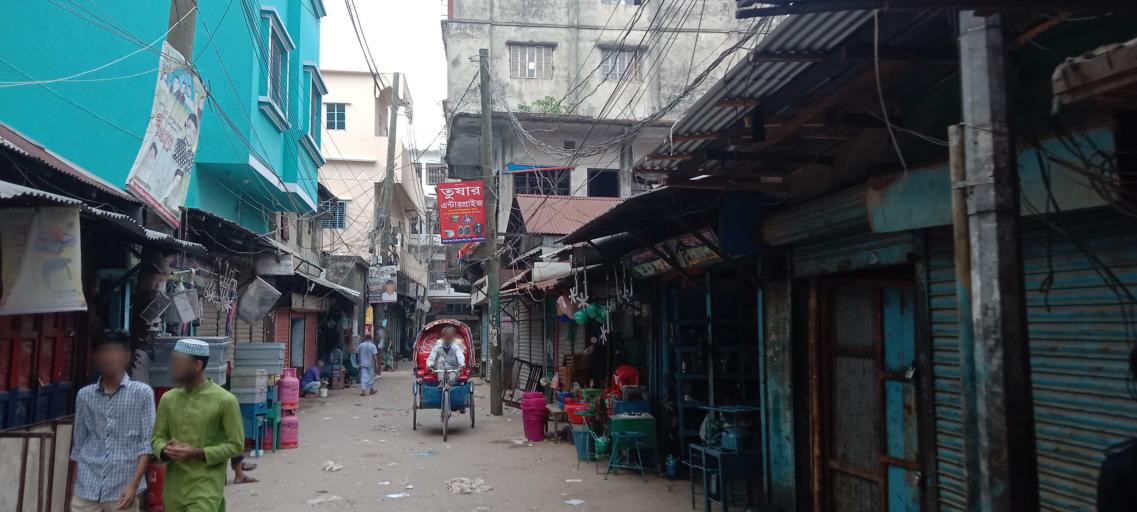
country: BD
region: Dhaka
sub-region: Dhaka
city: Dhaka
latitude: 23.7090
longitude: 90.3950
